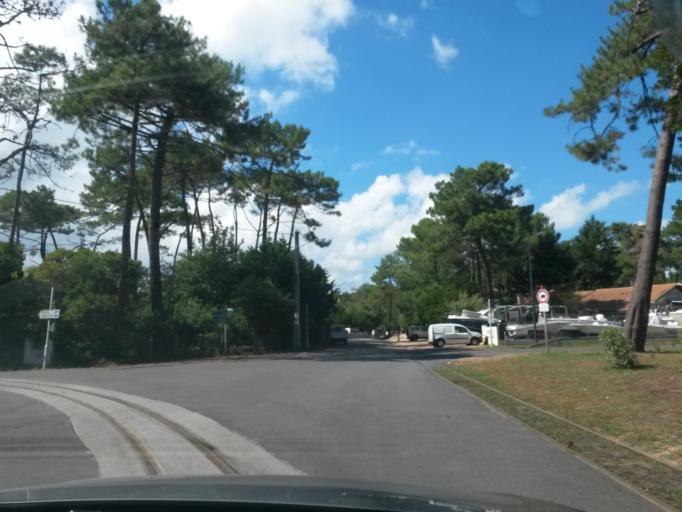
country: FR
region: Aquitaine
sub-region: Departement de la Gironde
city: Arcachon
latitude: 44.6583
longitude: -1.2443
